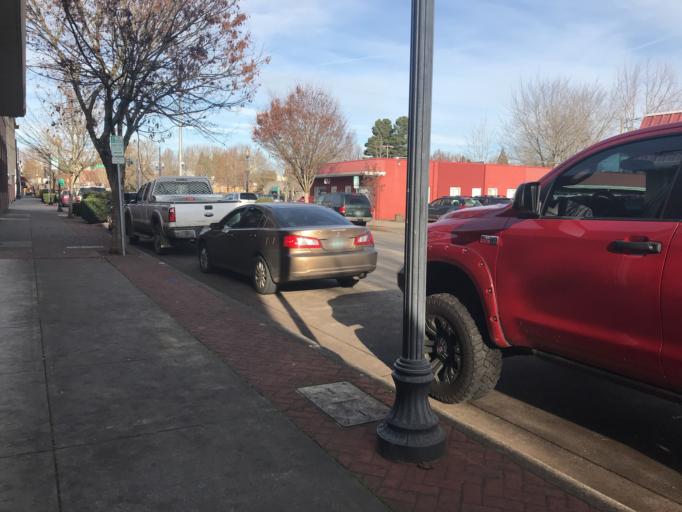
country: US
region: Oregon
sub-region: Washington County
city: Hillsboro
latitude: 45.5205
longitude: -122.9881
